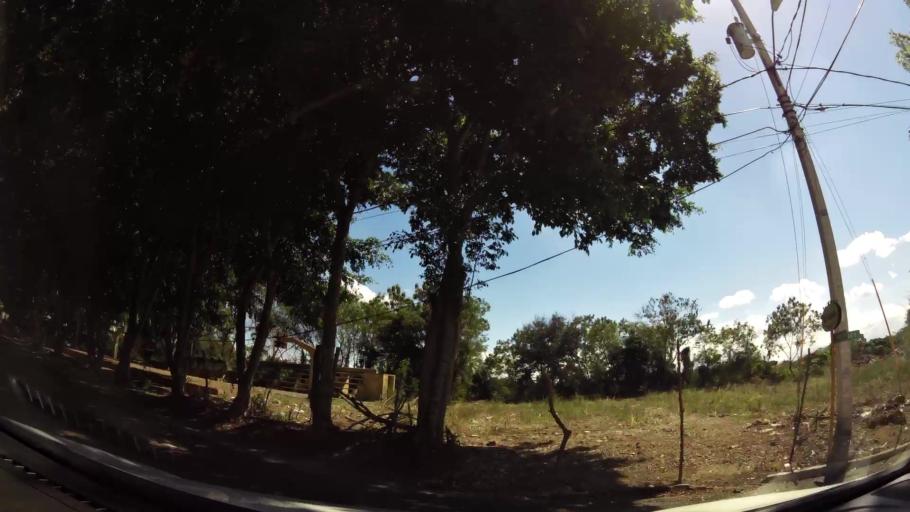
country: DO
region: Santiago
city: Santiago de los Caballeros
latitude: 19.4431
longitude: -70.6936
